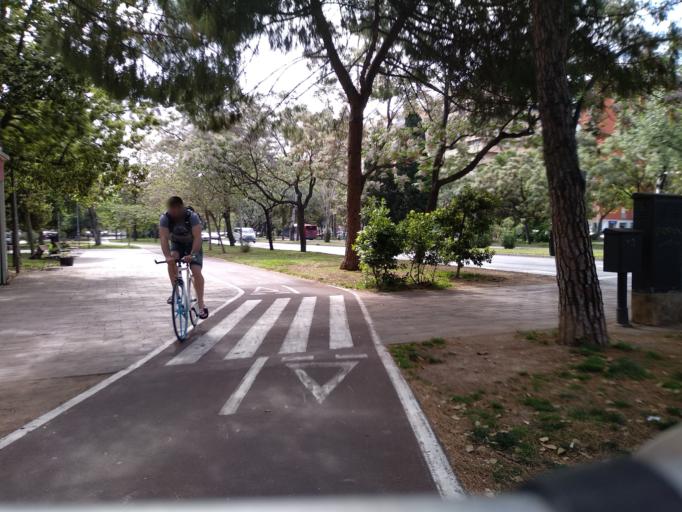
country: ES
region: Valencia
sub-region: Provincia de Valencia
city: Alboraya
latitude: 39.4749
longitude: -0.3504
